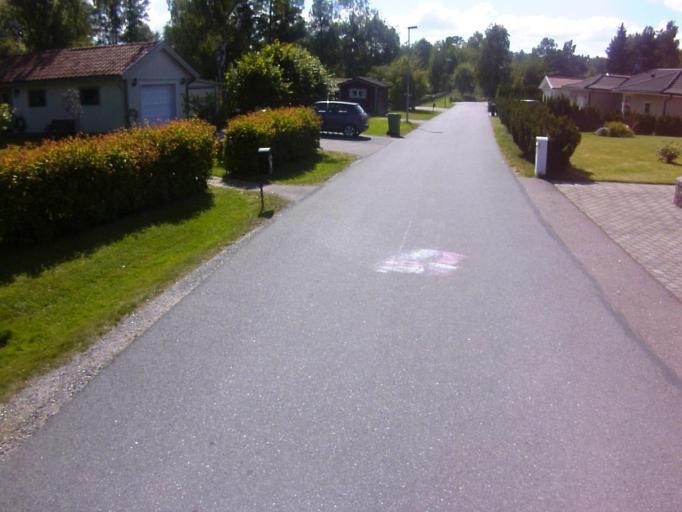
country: SE
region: Soedermanland
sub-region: Eskilstuna Kommun
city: Hallbybrunn
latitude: 59.3425
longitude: 16.4257
